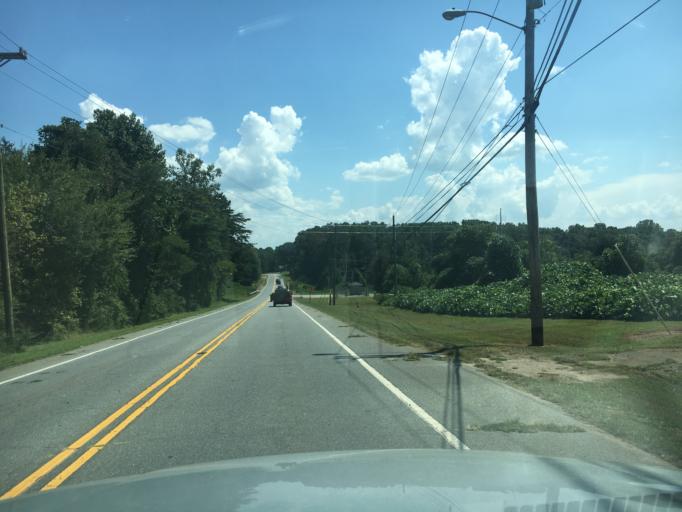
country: US
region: North Carolina
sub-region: Rutherford County
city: Forest City
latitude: 35.3038
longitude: -81.8566
